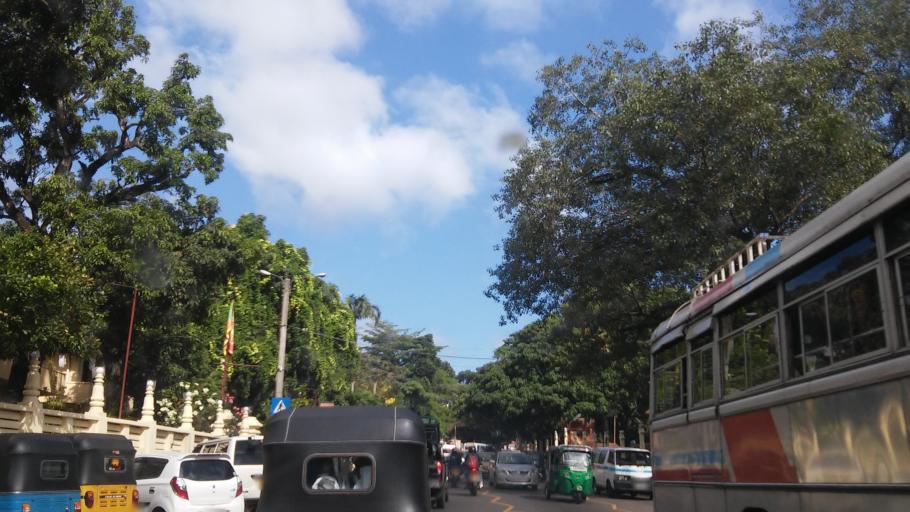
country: LK
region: Central
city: Kandy
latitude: 7.2675
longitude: 80.6009
